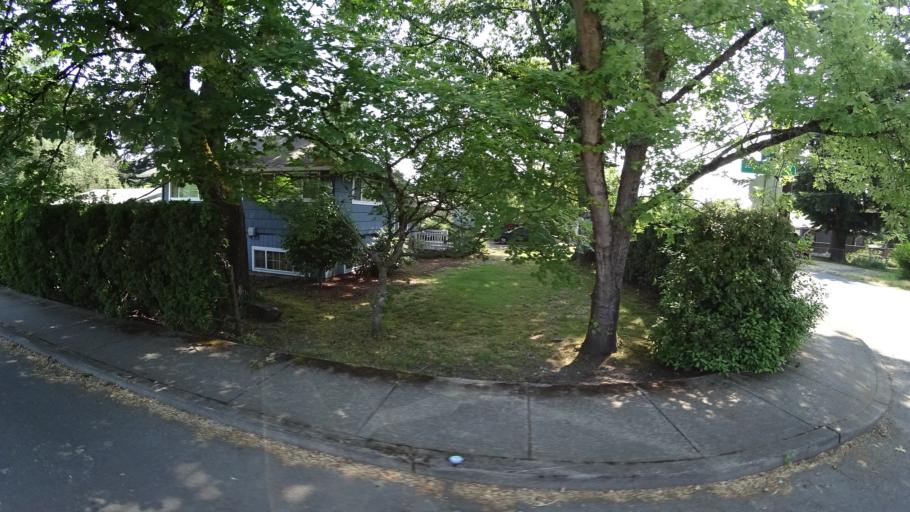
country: US
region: Oregon
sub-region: Clackamas County
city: Oatfield
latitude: 45.4447
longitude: -122.5989
